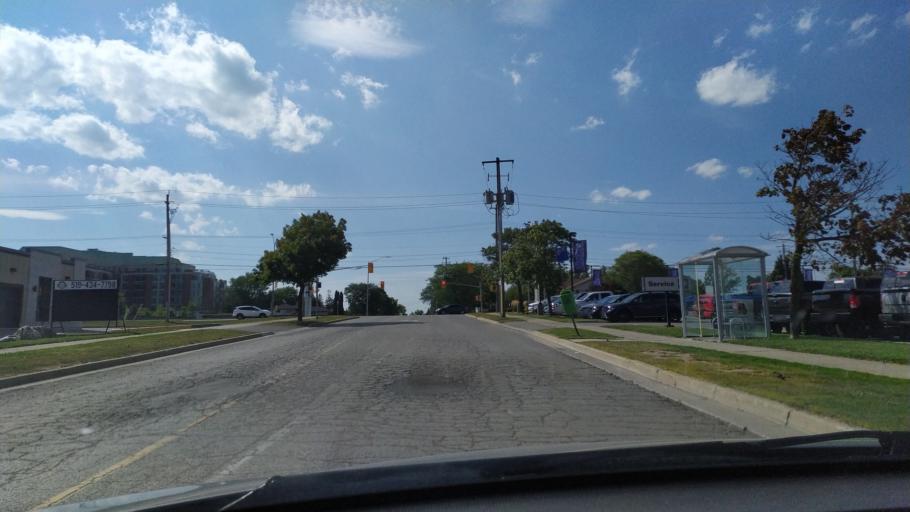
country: CA
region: Ontario
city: London
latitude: 42.9539
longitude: -81.2586
